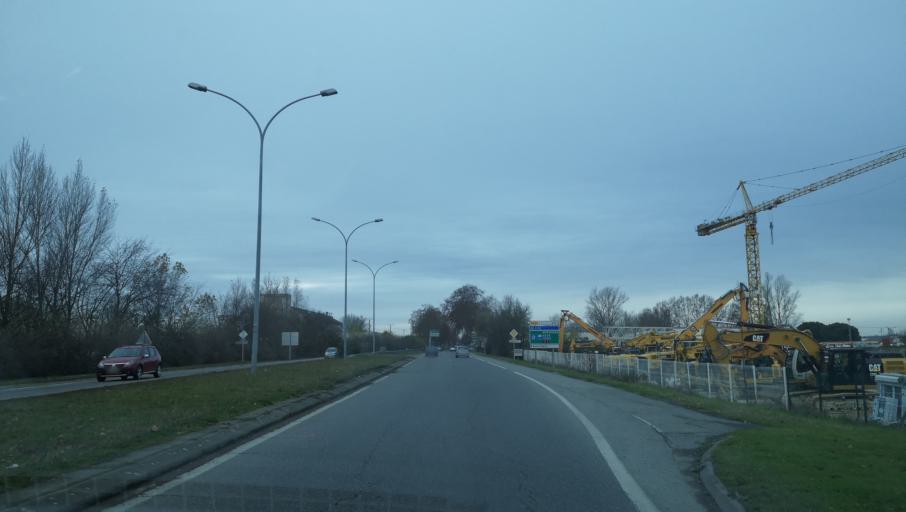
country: FR
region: Midi-Pyrenees
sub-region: Departement de la Haute-Garonne
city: Lespinasse
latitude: 43.7113
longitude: 1.3904
